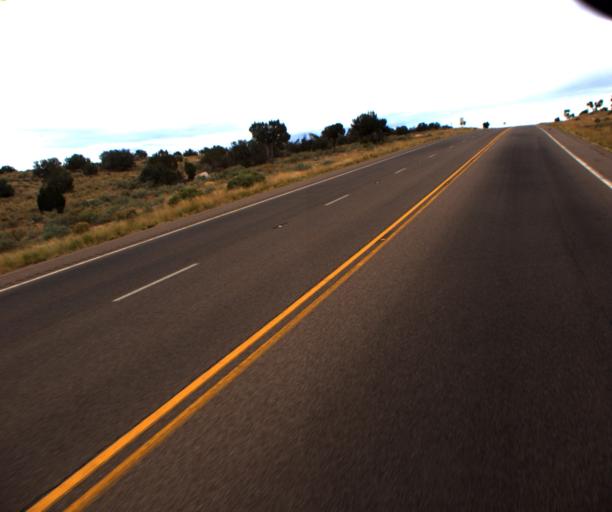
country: US
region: Arizona
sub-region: Navajo County
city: Snowflake
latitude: 34.5729
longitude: -110.0830
